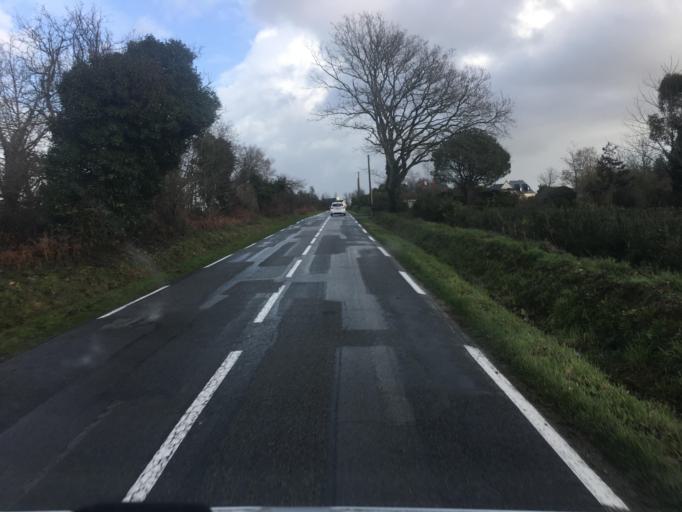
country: FR
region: Brittany
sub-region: Departement du Morbihan
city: Sarzeau
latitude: 47.5103
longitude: -2.7703
